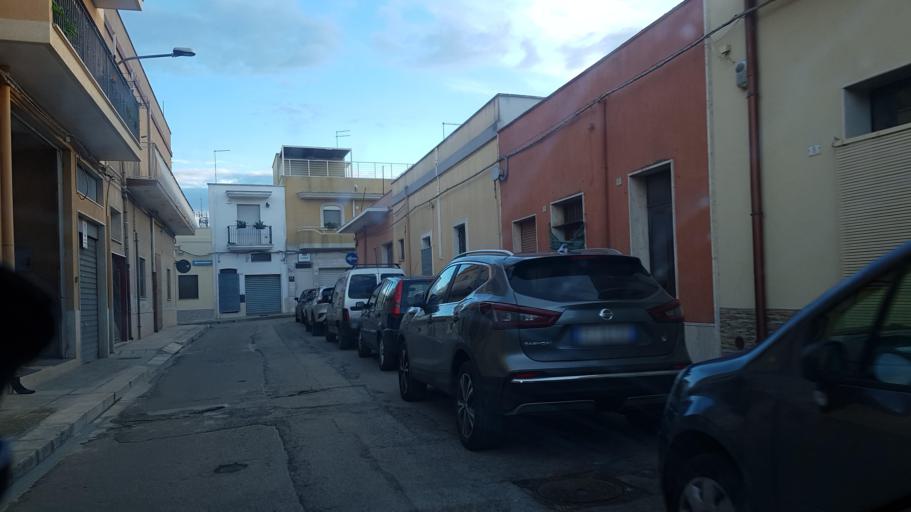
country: IT
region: Apulia
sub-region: Provincia di Brindisi
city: San Vito dei Normanni
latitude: 40.6600
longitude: 17.7067
